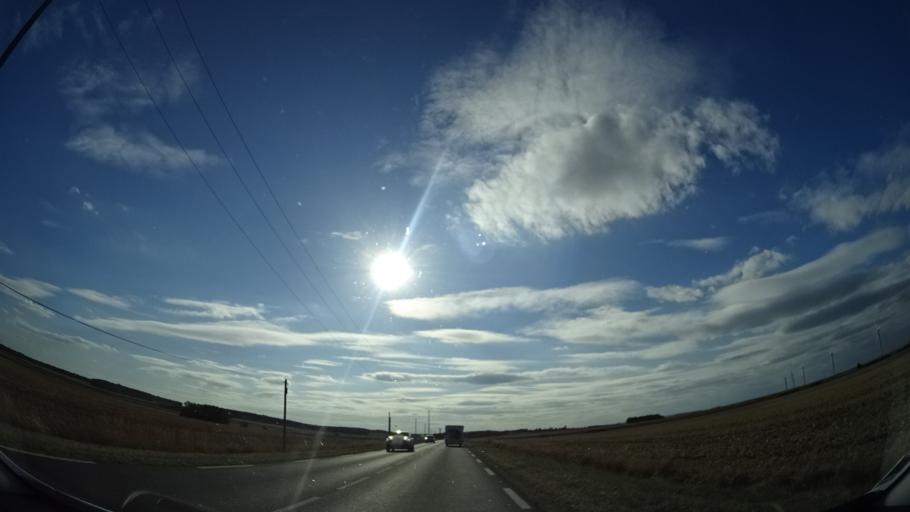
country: FR
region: Centre
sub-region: Departement du Loir-et-Cher
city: Oucques
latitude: 47.9043
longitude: 1.3665
